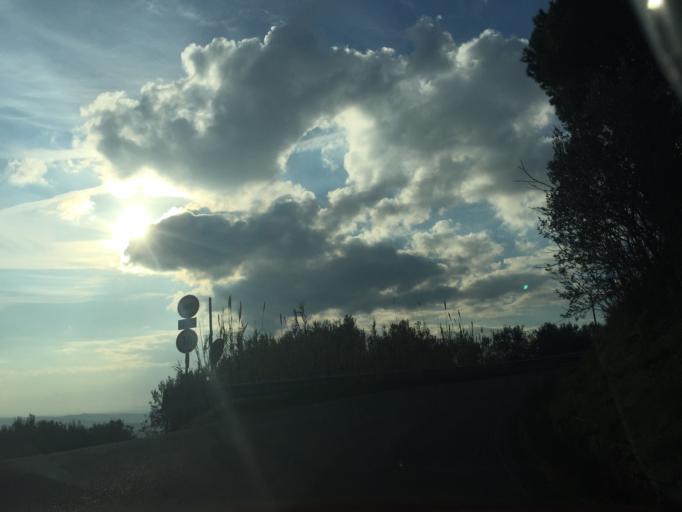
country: IT
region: Tuscany
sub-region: Province of Florence
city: Vinci
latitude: 43.8060
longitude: 10.9291
